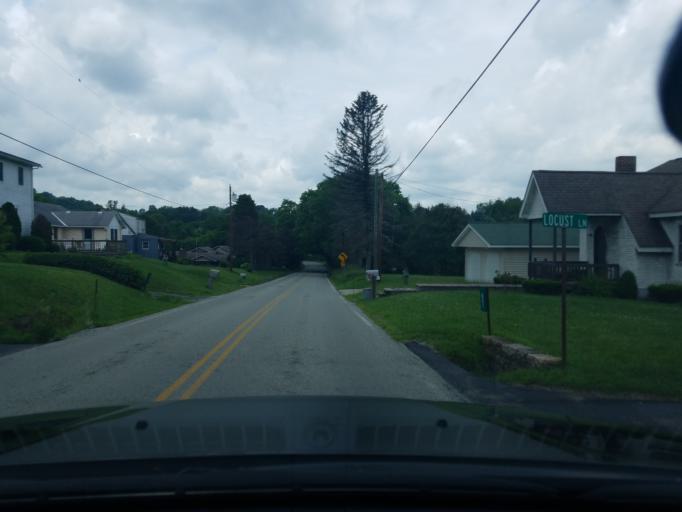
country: US
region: Pennsylvania
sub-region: Westmoreland County
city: Youngwood
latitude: 40.2185
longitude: -79.5438
